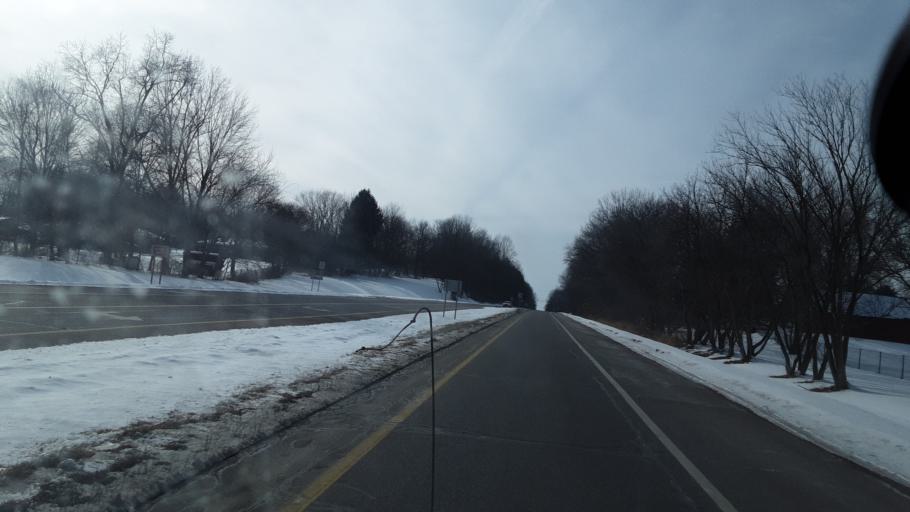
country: US
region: Ohio
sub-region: Summit County
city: Mogadore
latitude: 41.0273
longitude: -81.3480
